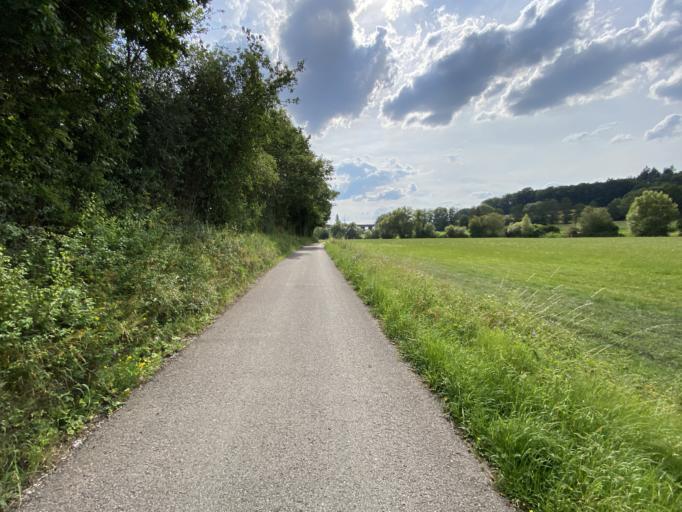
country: DE
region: Bavaria
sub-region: Regierungsbezirk Mittelfranken
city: Obermichelbach
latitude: 49.5653
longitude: 10.9534
